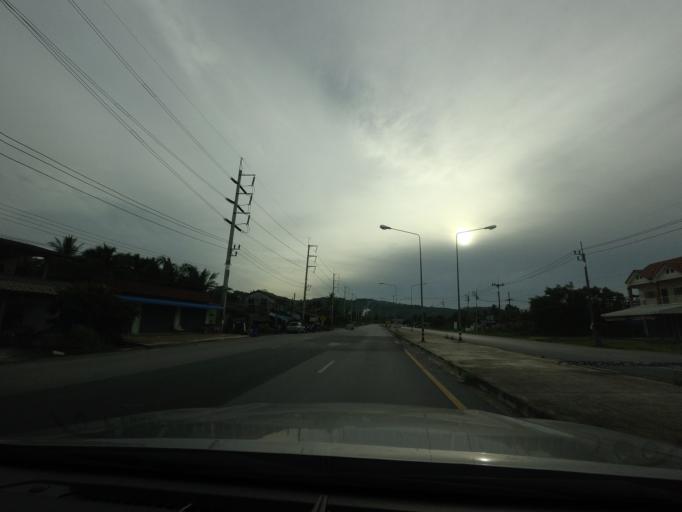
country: TH
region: Nakhon Si Thammarat
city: Hua Sai
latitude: 8.0514
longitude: 100.2158
